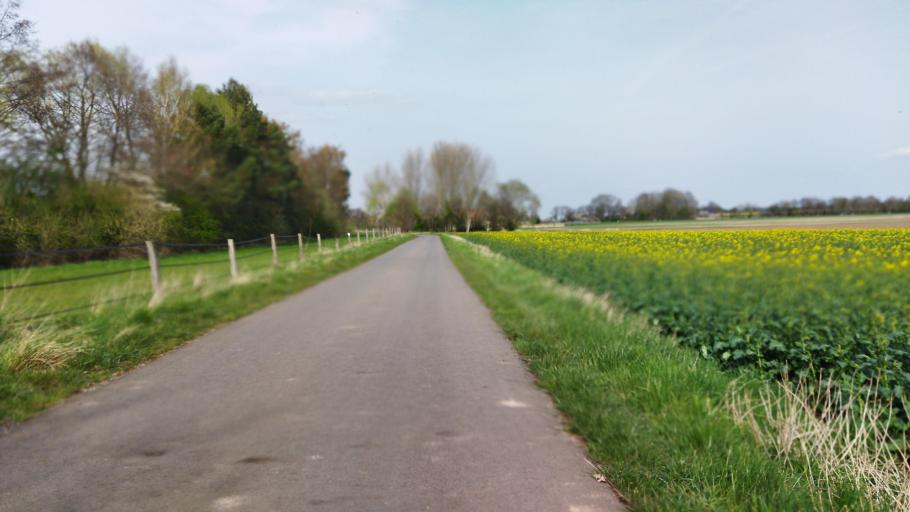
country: DE
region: Lower Saxony
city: Raddestorf
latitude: 52.4395
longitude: 8.9837
